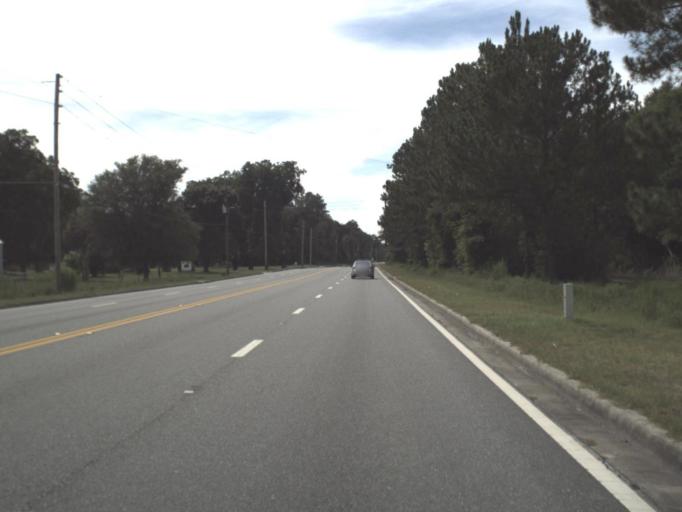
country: US
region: Florida
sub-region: Taylor County
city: Perry
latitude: 30.0943
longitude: -83.5433
